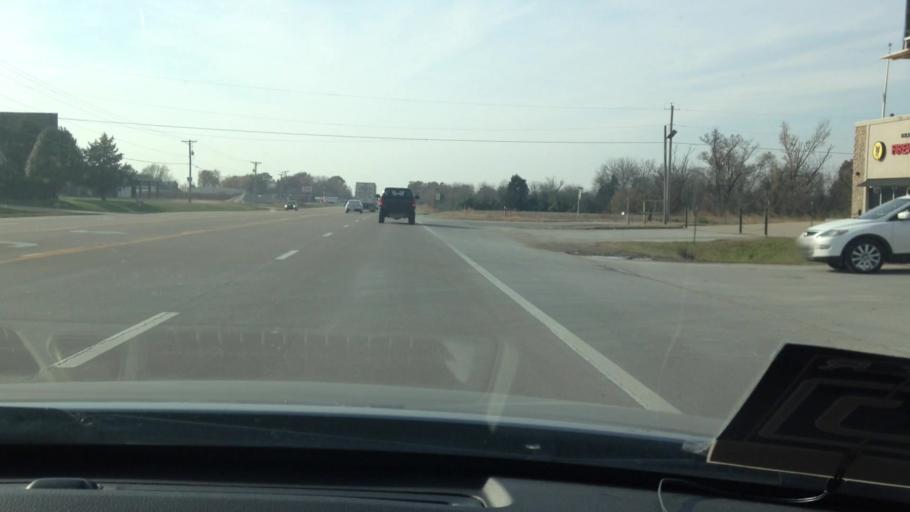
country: US
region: Missouri
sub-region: Henry County
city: Clinton
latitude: 38.3893
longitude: -93.7964
